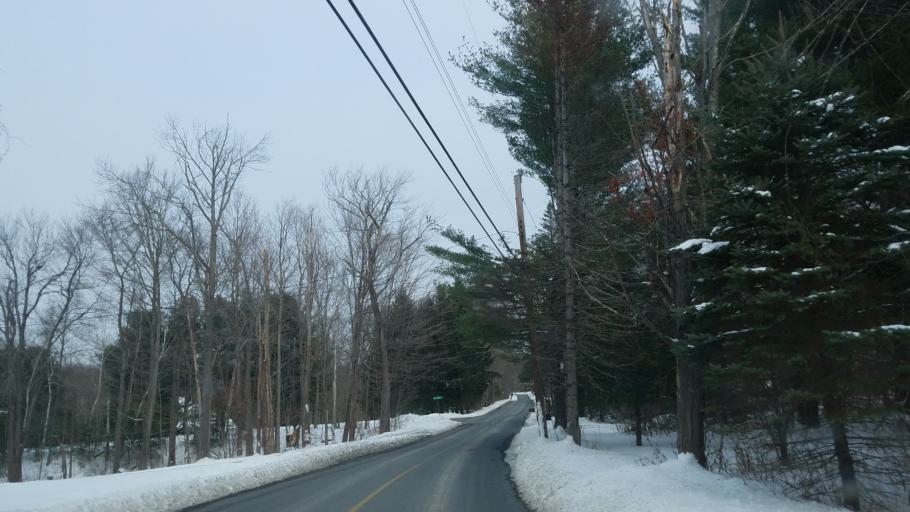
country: US
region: Connecticut
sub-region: Litchfield County
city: New Hartford Center
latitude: 41.8821
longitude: -73.0144
